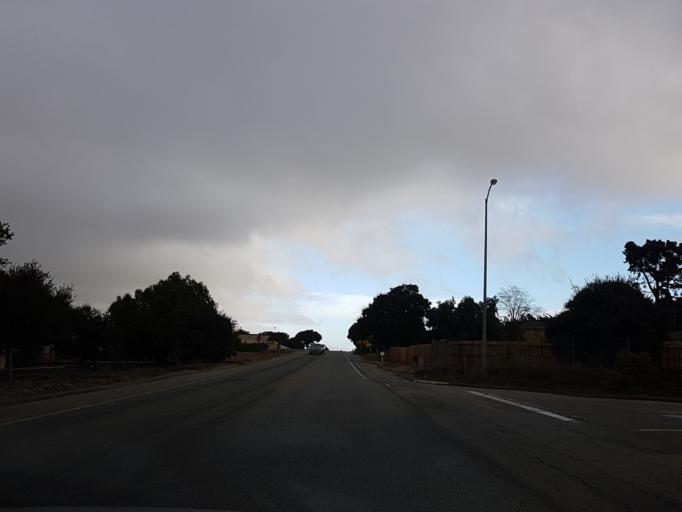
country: US
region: California
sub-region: Monterey County
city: Salinas
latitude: 36.6003
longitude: -121.6312
